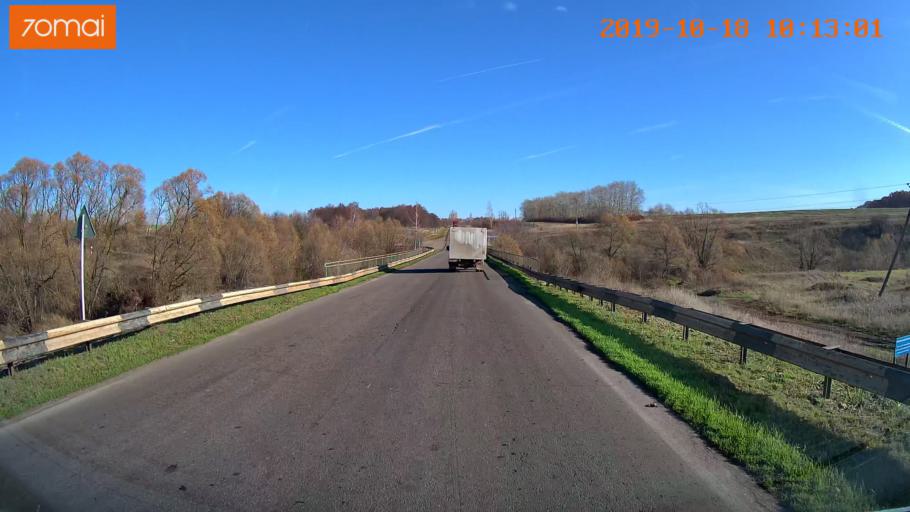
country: RU
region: Tula
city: Kurkino
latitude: 53.3982
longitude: 38.5158
